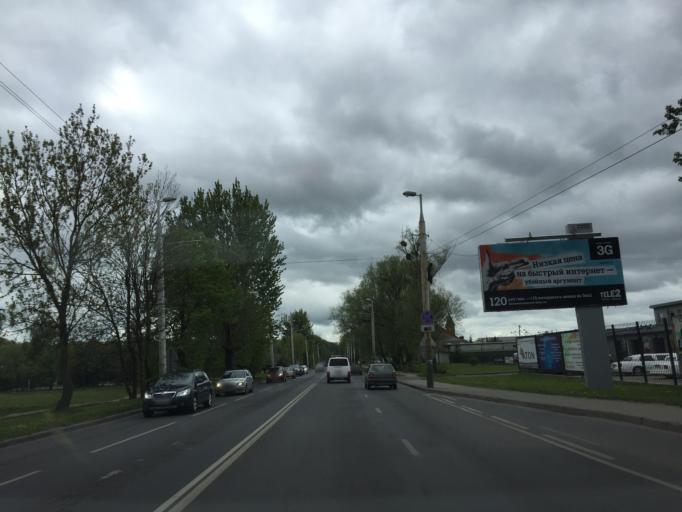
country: RU
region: Kaliningrad
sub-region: Gorod Kaliningrad
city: Kaliningrad
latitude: 54.6901
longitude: 20.4660
